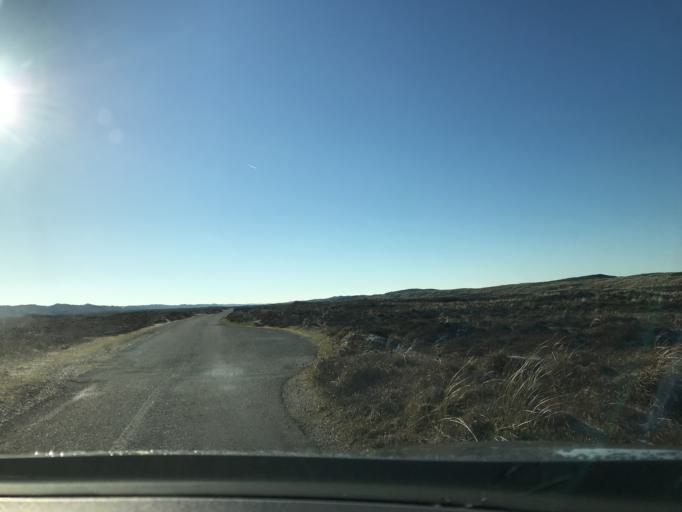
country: DK
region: South Denmark
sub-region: Varde Kommune
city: Oksbol
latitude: 55.7997
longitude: 8.1819
